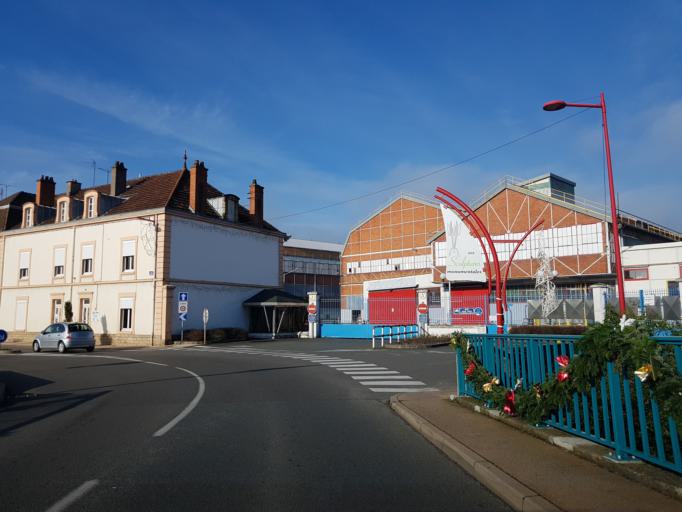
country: FR
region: Bourgogne
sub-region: Departement de Saone-et-Loire
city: Gueugnon
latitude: 46.6009
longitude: 4.0649
